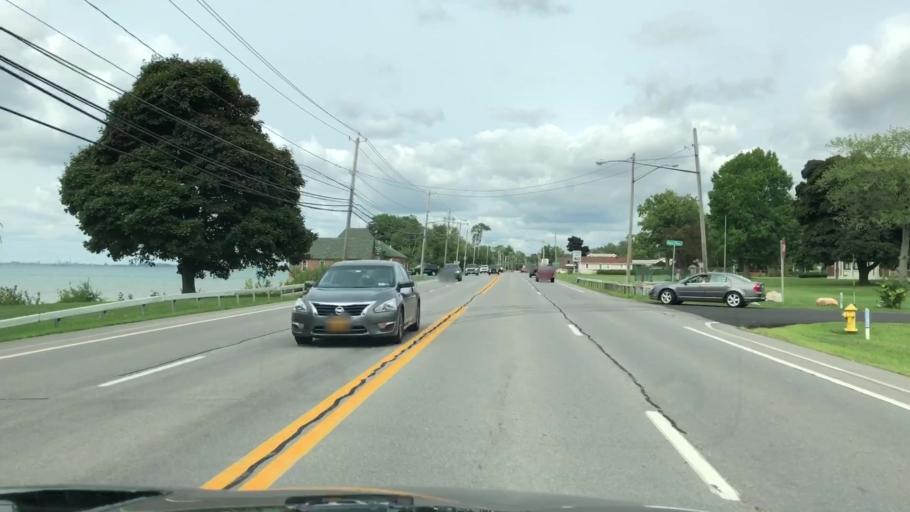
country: US
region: New York
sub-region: Erie County
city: Wanakah
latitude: 42.7470
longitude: -78.9017
